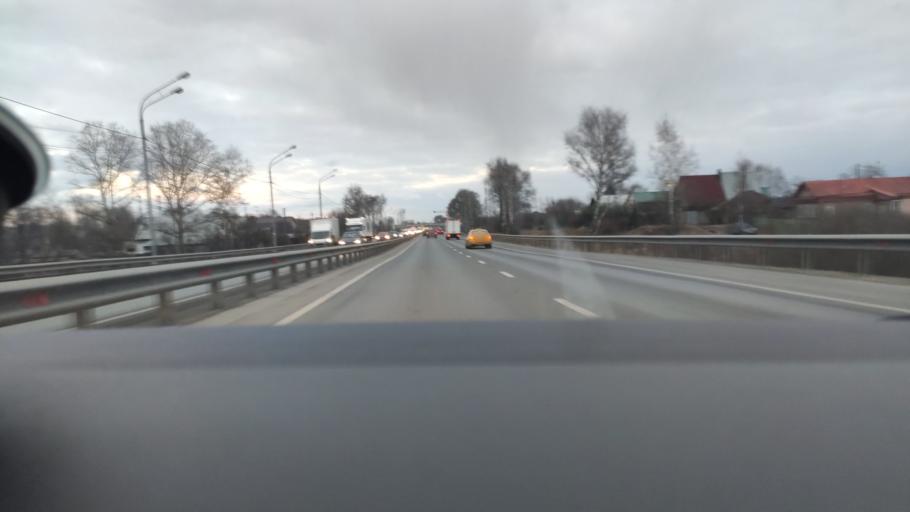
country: RU
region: Moskovskaya
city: Obukhovo
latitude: 55.8333
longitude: 38.3586
